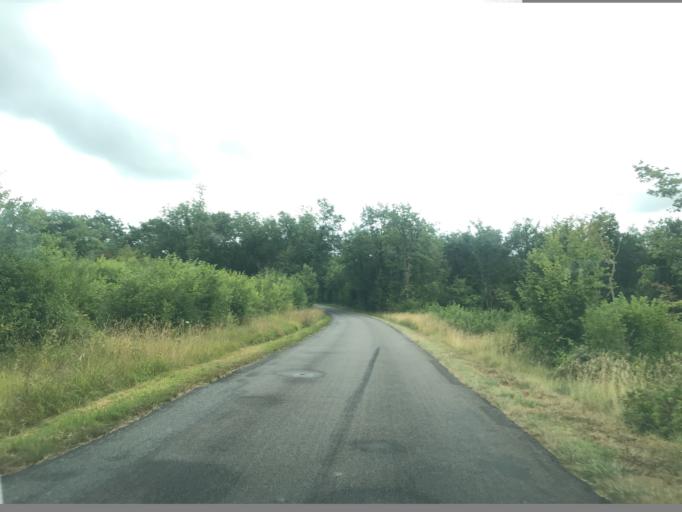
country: FR
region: Poitou-Charentes
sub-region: Departement de la Charente
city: Dignac
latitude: 45.5582
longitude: 0.2424
